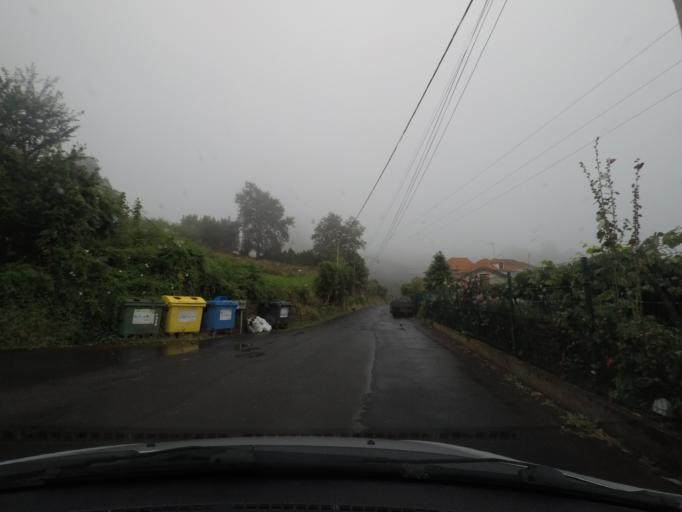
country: PT
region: Madeira
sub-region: Santana
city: Santana
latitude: 32.7949
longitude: -16.8763
